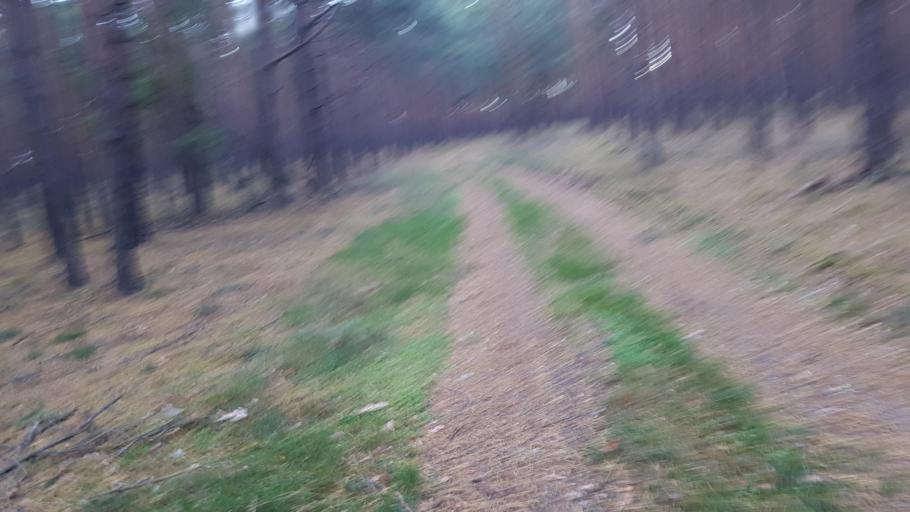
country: DE
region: Brandenburg
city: Falkenberg
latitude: 51.6473
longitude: 13.3047
